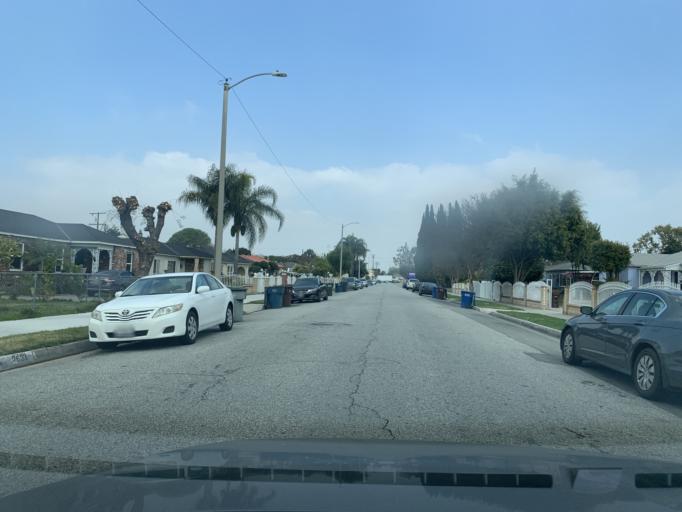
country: US
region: California
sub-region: Los Angeles County
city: South El Monte
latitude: 34.0599
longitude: -118.0448
